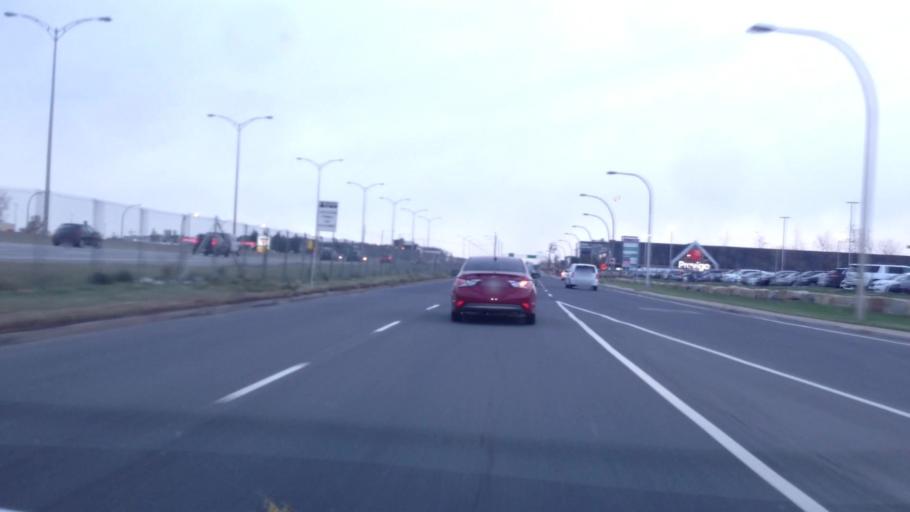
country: CA
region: Quebec
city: Kirkland
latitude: 45.4533
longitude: -73.8559
